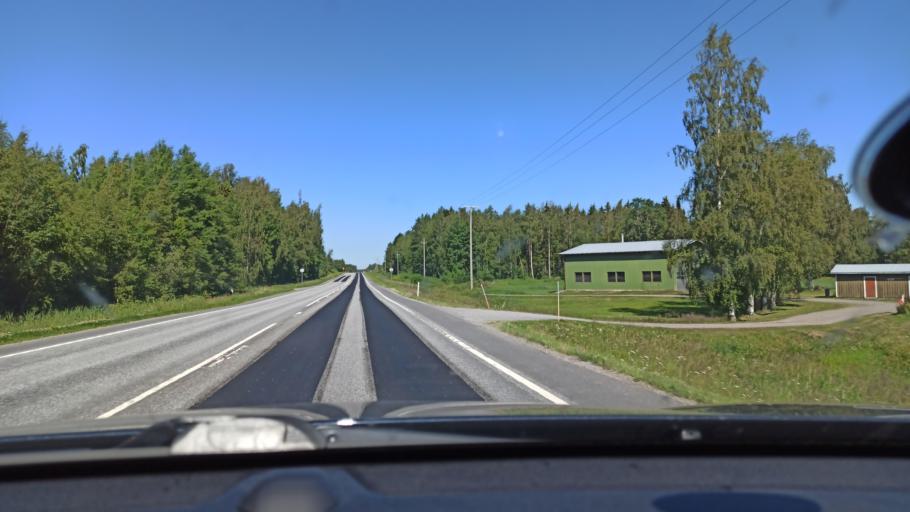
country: FI
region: Ostrobothnia
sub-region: Vaasa
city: Voera
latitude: 63.2317
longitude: 22.2453
